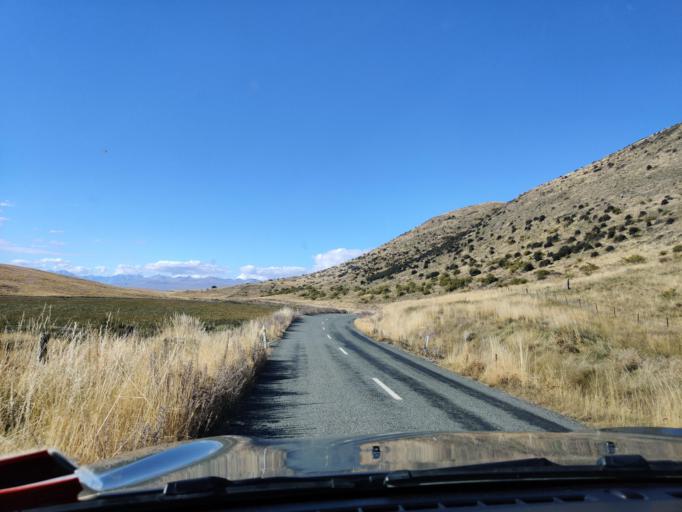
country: NZ
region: Canterbury
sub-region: Timaru District
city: Pleasant Point
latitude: -43.9797
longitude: 170.4611
